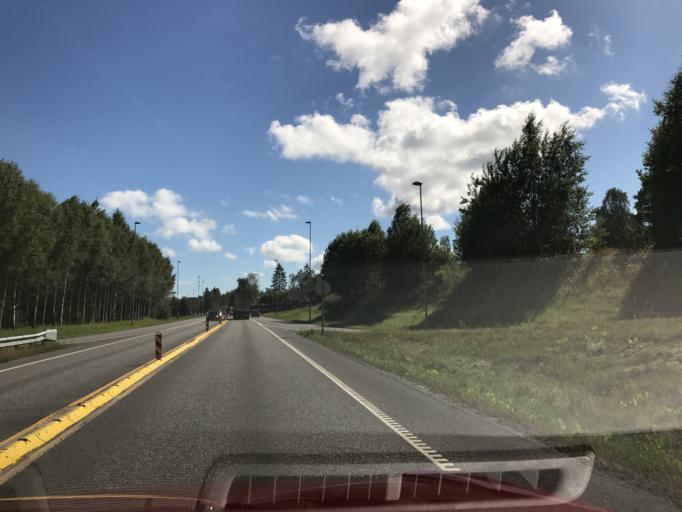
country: NO
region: Telemark
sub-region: Bamble
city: Langesund
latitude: 59.0351
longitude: 9.6765
